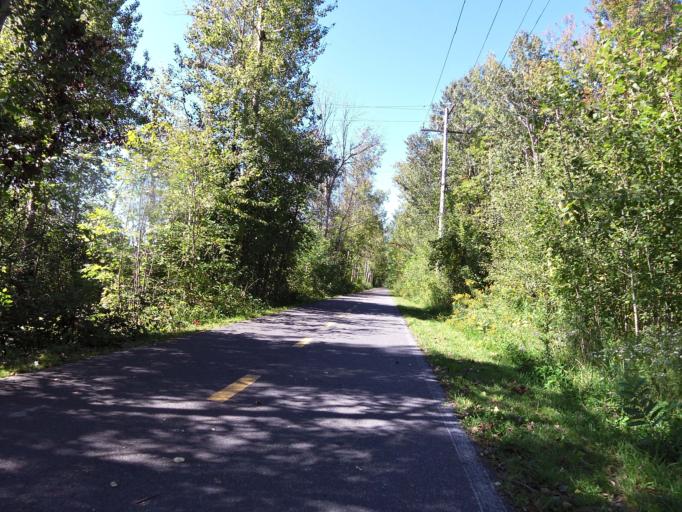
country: CA
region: Ontario
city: Bourget
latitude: 45.2714
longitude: -75.3035
